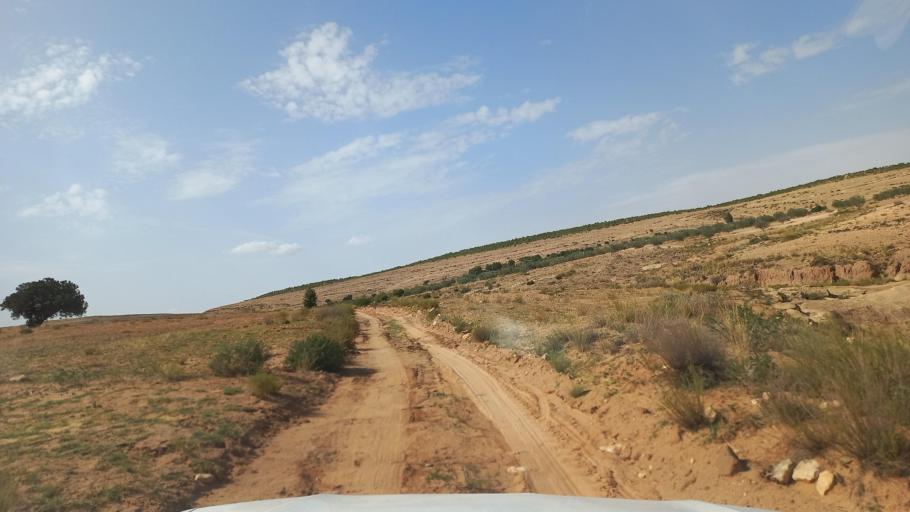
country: TN
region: Al Qasrayn
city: Kasserine
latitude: 35.3632
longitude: 8.8596
